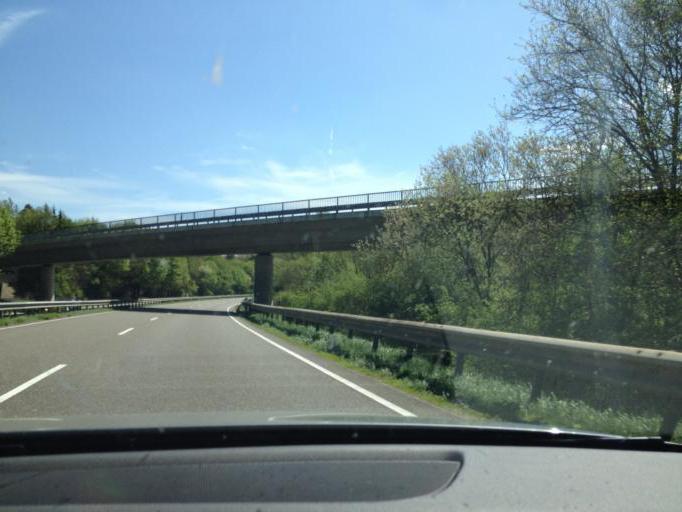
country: DE
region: Rheinland-Pfalz
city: Kerschenbach
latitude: 50.3692
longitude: 6.5101
